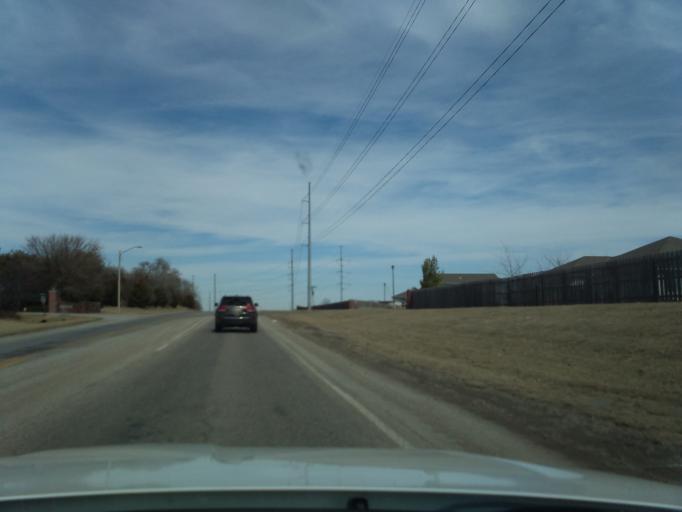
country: US
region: Nebraska
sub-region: Lancaster County
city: Lincoln
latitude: 40.7312
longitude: -96.6443
